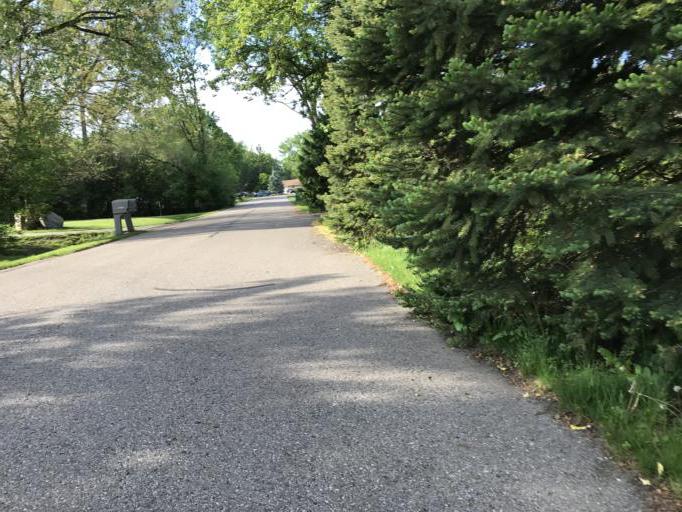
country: US
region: Michigan
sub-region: Oakland County
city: Farmington
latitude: 42.4760
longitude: -83.3447
